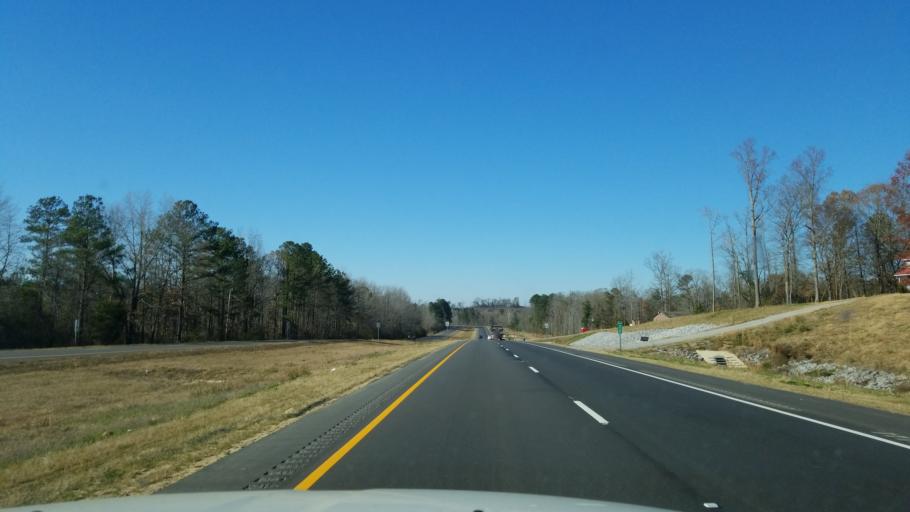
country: US
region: Alabama
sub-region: Pickens County
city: Reform
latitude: 33.3653
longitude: -87.9804
